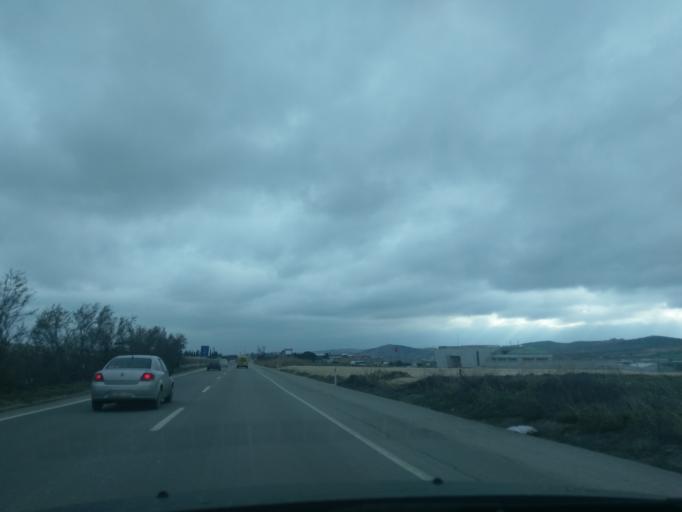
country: TR
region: Istanbul
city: Muratbey
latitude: 41.1039
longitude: 28.5073
